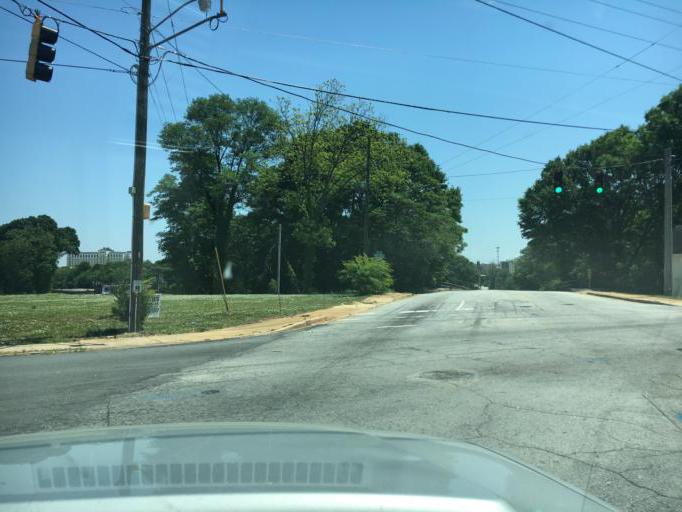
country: US
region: South Carolina
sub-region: Spartanburg County
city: Spartanburg
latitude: 34.9506
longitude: -81.9426
